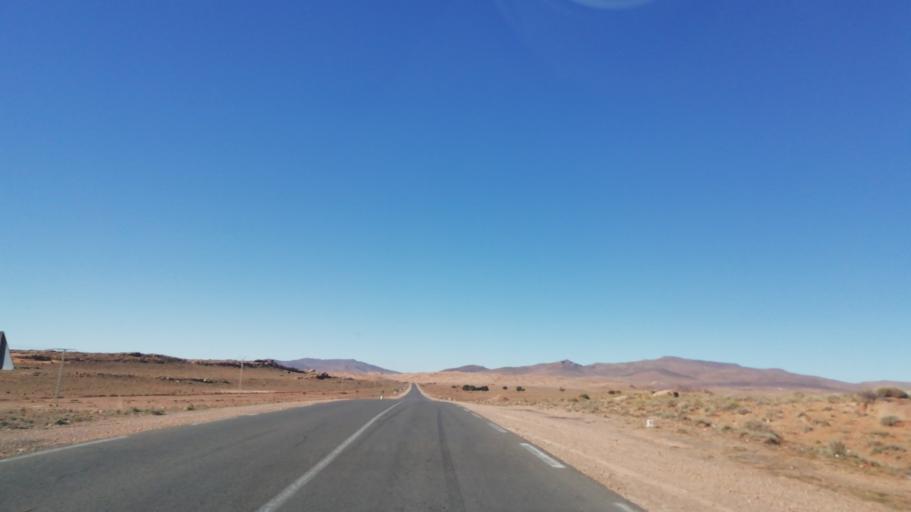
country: DZ
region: El Bayadh
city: El Bayadh
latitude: 33.6149
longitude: 1.2146
